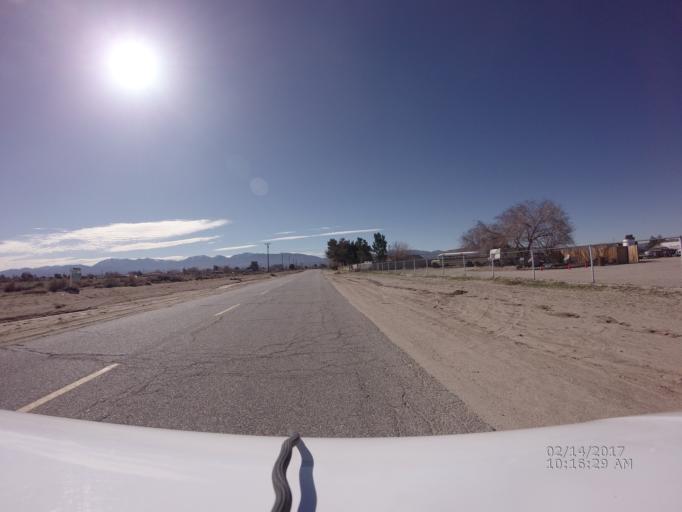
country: US
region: California
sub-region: Los Angeles County
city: Littlerock
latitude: 34.5830
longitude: -117.9517
